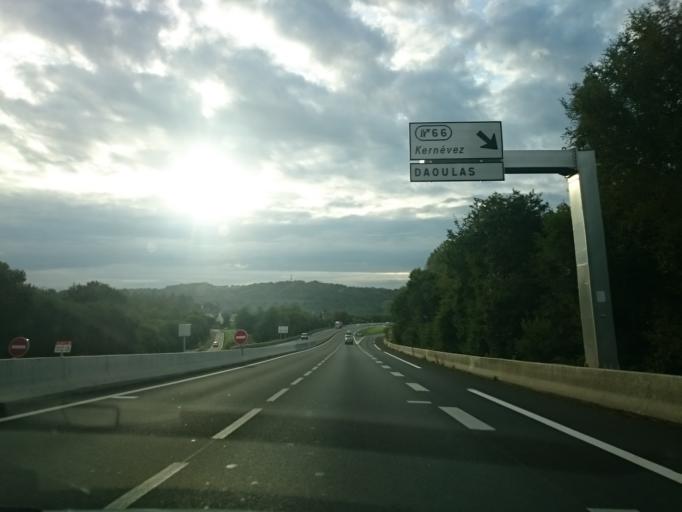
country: FR
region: Brittany
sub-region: Departement du Finistere
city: Daoulas
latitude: 48.3693
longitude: -4.2629
